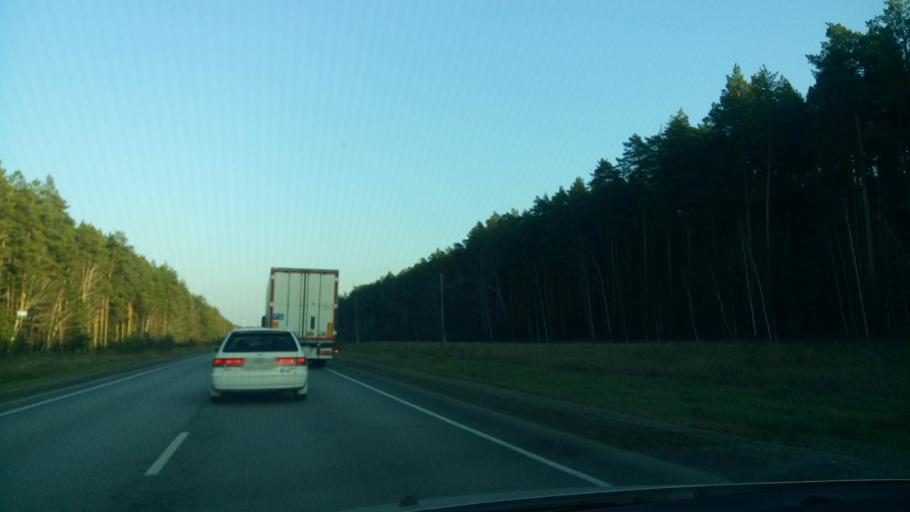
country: RU
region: Sverdlovsk
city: Gryaznovskoye
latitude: 56.7855
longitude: 61.6736
